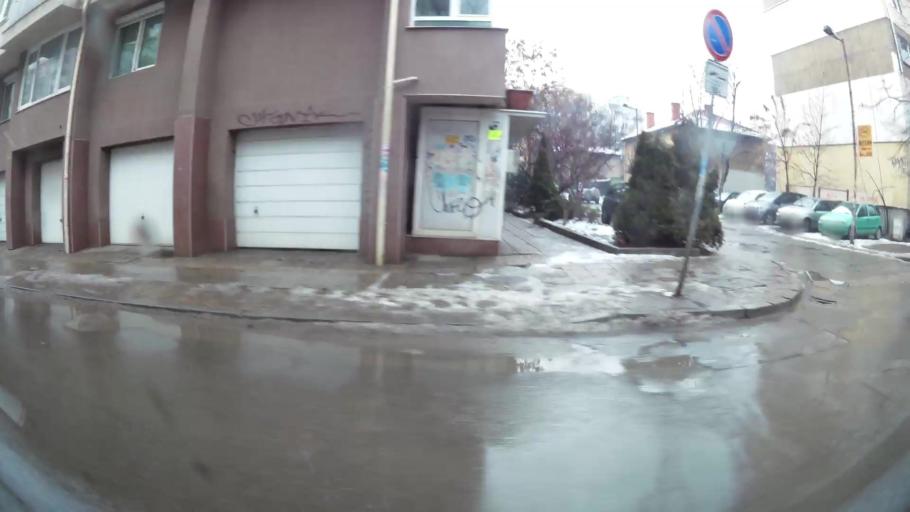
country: BG
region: Sofia-Capital
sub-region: Stolichna Obshtina
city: Sofia
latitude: 42.6616
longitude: 23.3015
